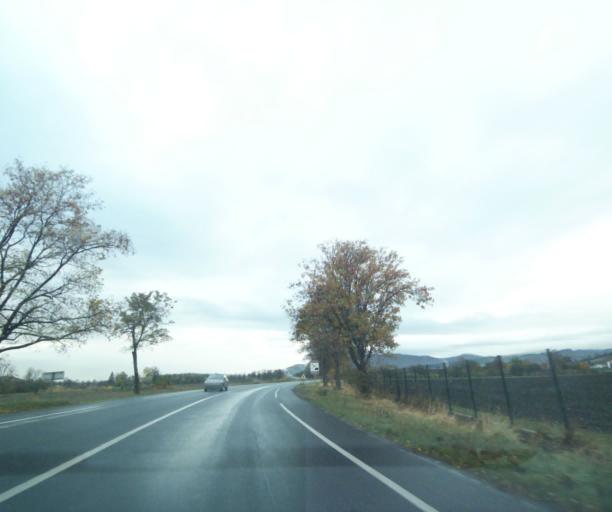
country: FR
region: Auvergne
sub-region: Departement du Puy-de-Dome
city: Aulnat
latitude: 45.7776
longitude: 3.1480
